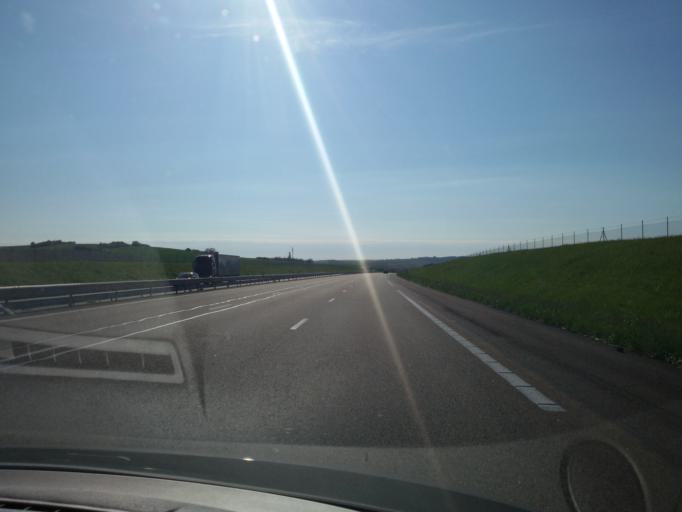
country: FR
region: Bourgogne
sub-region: Departement de l'Yonne
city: Aillant-sur-Tholon
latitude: 47.8947
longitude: 3.3996
